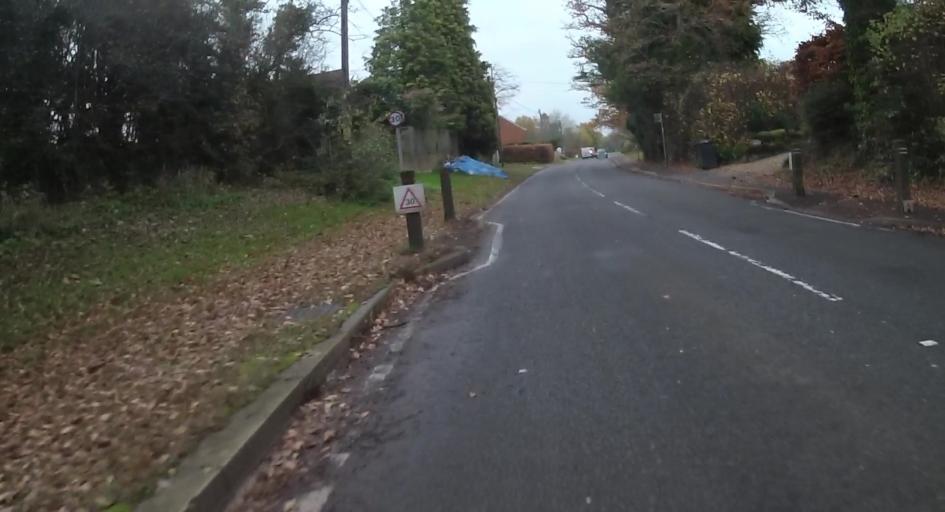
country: GB
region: England
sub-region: West Berkshire
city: Stratfield Mortimer
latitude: 51.3278
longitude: -1.0704
